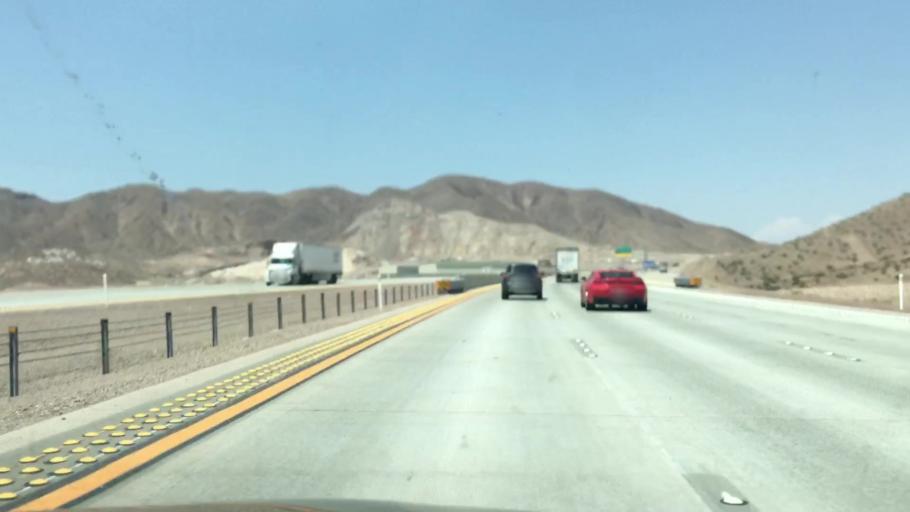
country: US
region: Nevada
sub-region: Clark County
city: Boulder City
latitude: 35.9565
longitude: -114.9082
